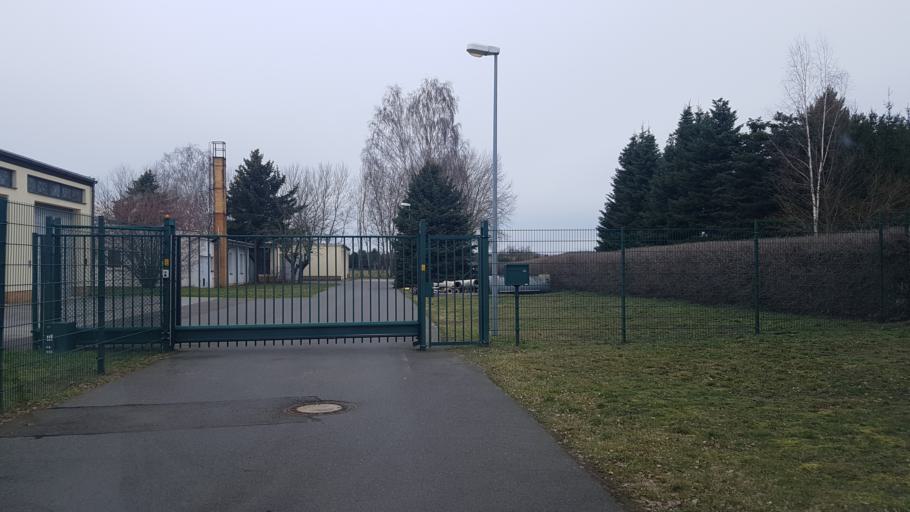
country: DE
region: Brandenburg
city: Finsterwalde
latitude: 51.6185
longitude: 13.7022
